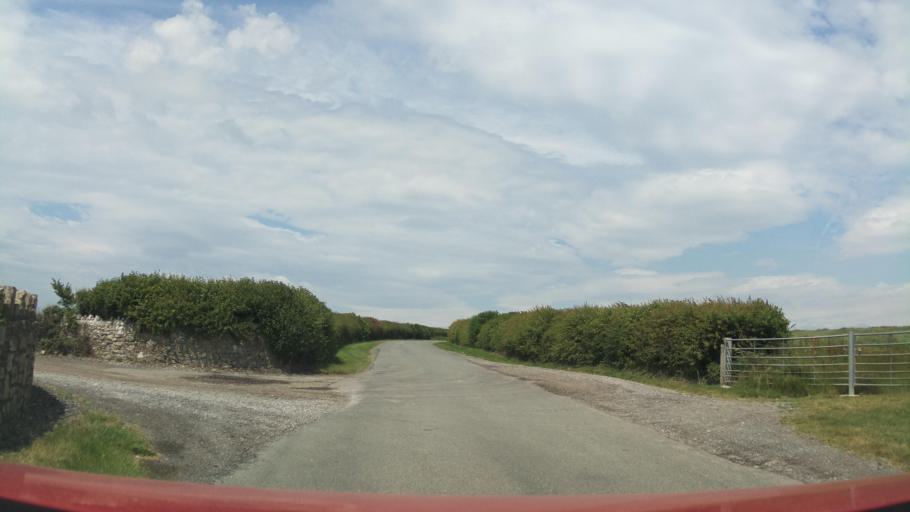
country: GB
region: Wales
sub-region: Vale of Glamorgan
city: Wick
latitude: 51.4399
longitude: -3.5685
